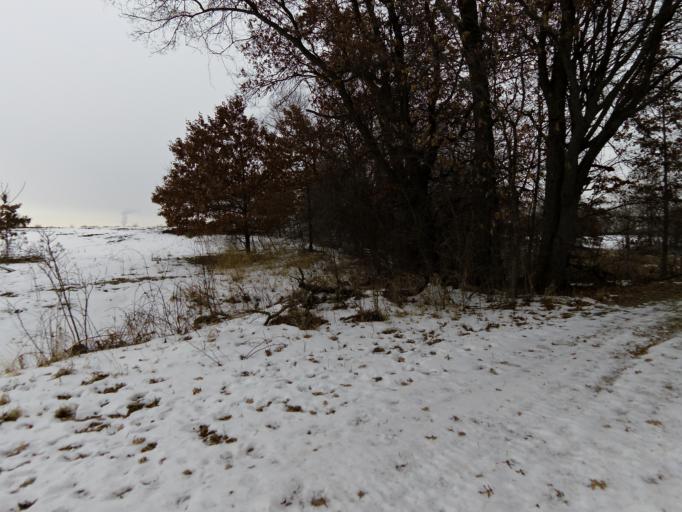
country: US
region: Minnesota
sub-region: Washington County
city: Lake Elmo
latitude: 44.9852
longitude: -92.9009
